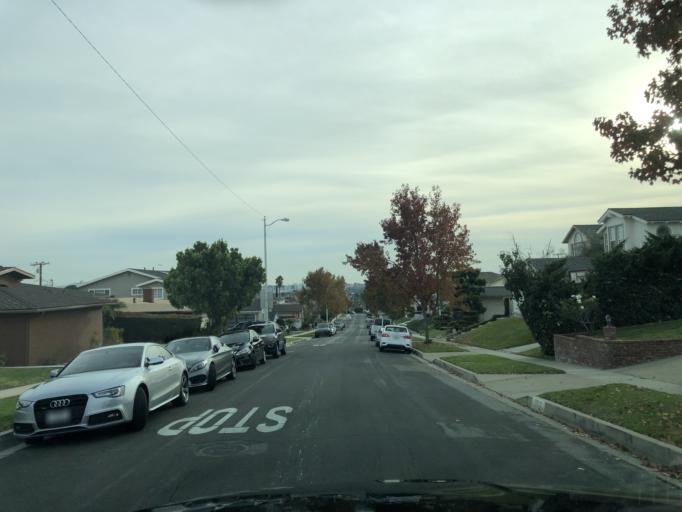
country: US
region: California
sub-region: Los Angeles County
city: Ladera Heights
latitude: 33.9910
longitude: -118.3704
